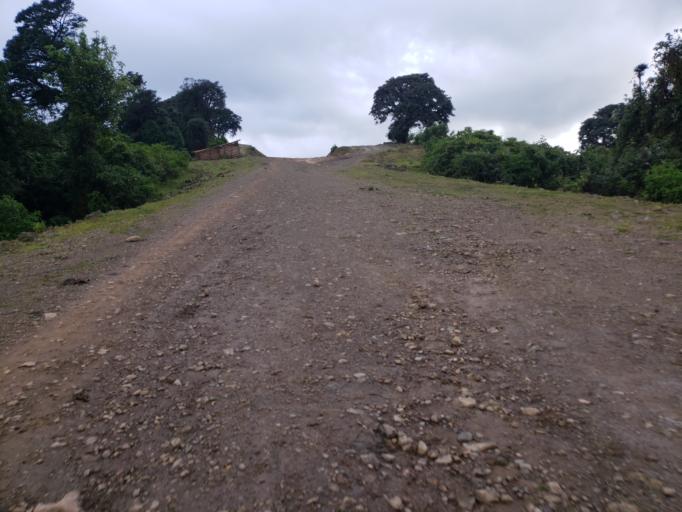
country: ET
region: Oromiya
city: Dodola
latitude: 6.6600
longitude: 39.3638
